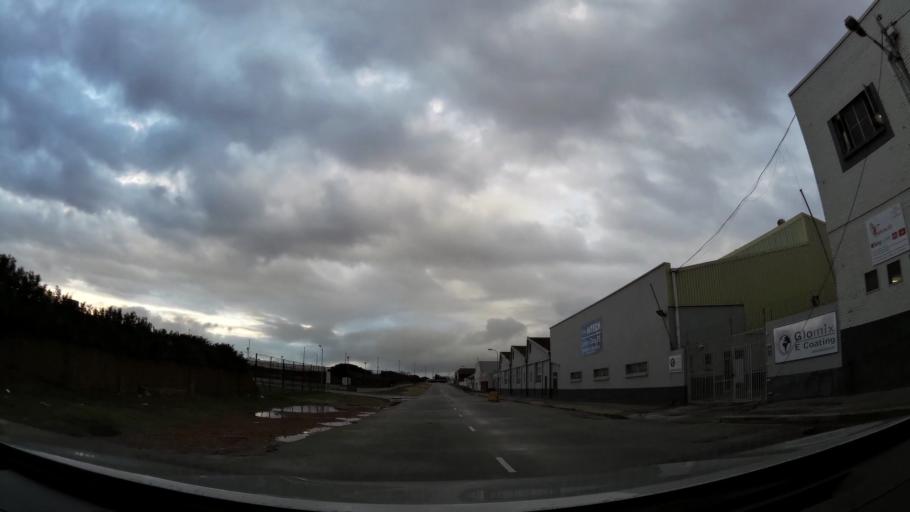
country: ZA
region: Eastern Cape
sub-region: Nelson Mandela Bay Metropolitan Municipality
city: Port Elizabeth
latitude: -33.9266
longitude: 25.6071
